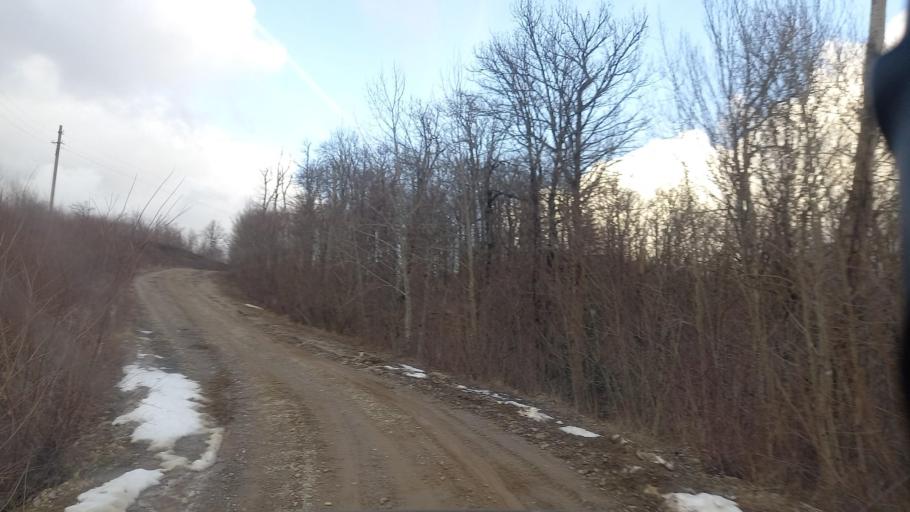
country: RU
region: Krasnodarskiy
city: Dzhubga
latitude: 44.5067
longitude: 38.7705
